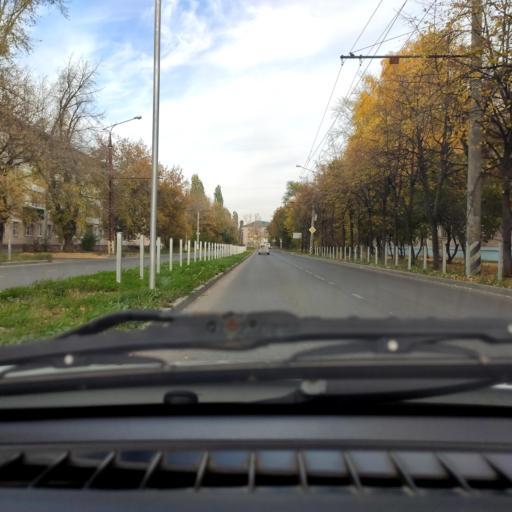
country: RU
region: Samara
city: Tol'yatti
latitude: 53.5203
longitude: 49.4085
